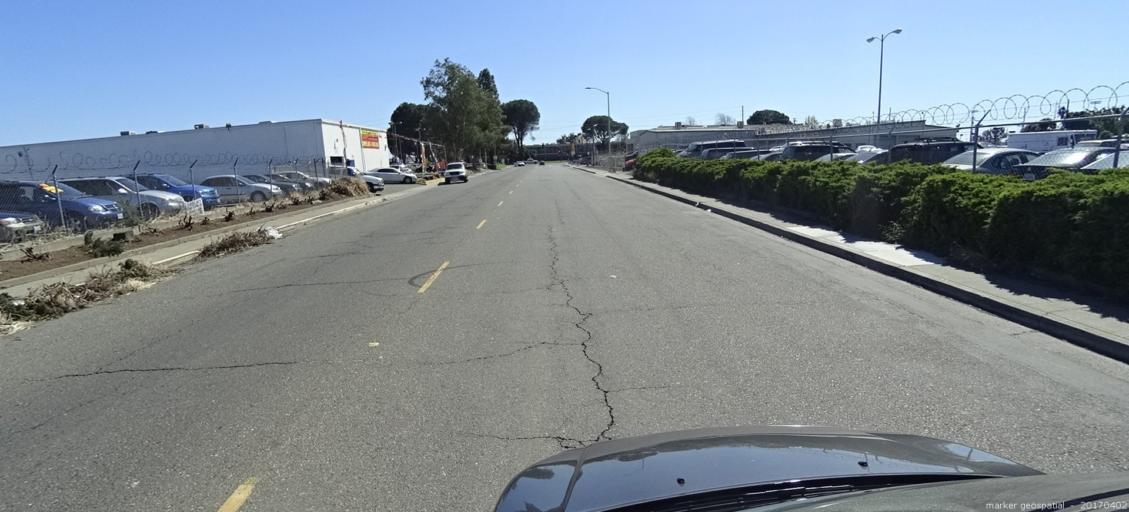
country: US
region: California
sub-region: Sacramento County
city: Parkway
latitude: 38.4978
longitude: -121.4654
